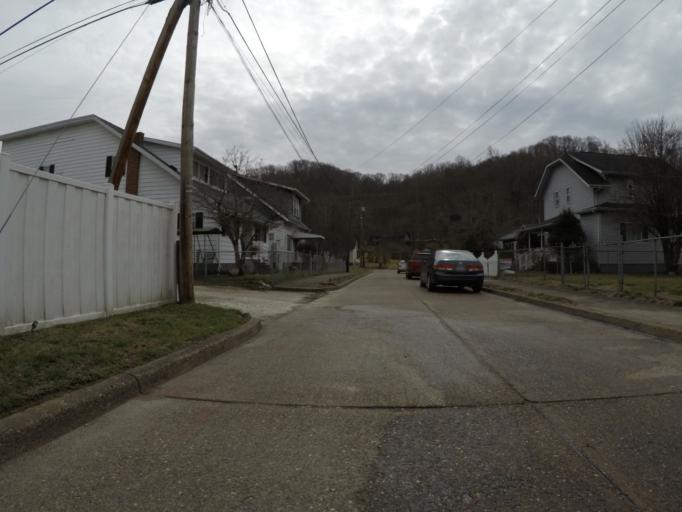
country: US
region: Ohio
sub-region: Lawrence County
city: Burlington
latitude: 38.3990
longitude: -82.5084
